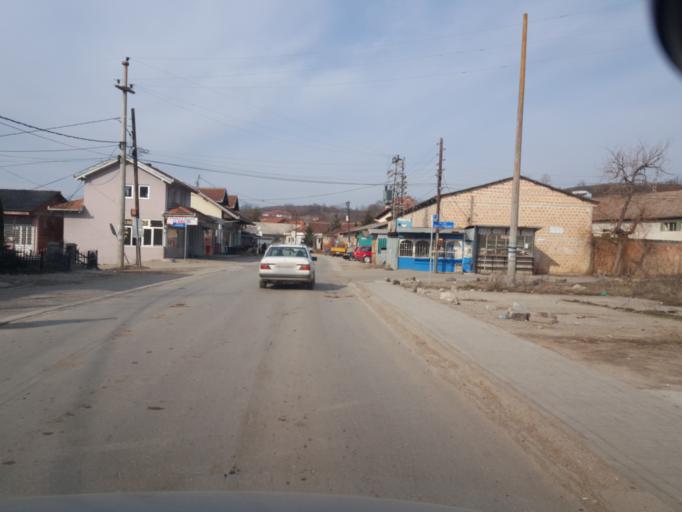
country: XK
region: Pec
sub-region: Komuna e Klines
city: Klina
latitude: 42.6621
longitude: 20.5395
